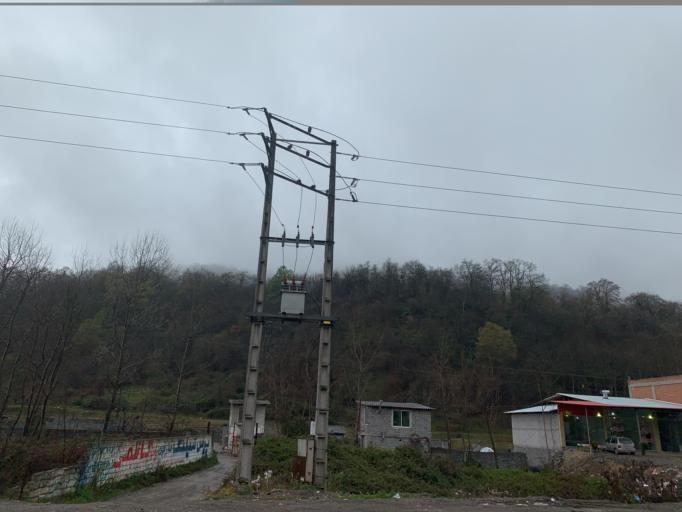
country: IR
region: Mazandaran
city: Amol
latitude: 36.3722
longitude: 52.3536
